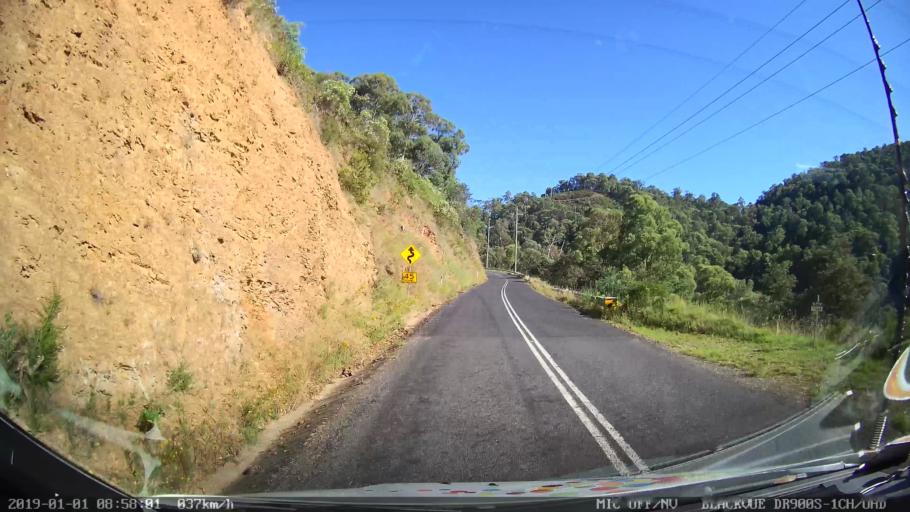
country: AU
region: New South Wales
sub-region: Snowy River
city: Jindabyne
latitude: -36.2464
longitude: 148.1881
